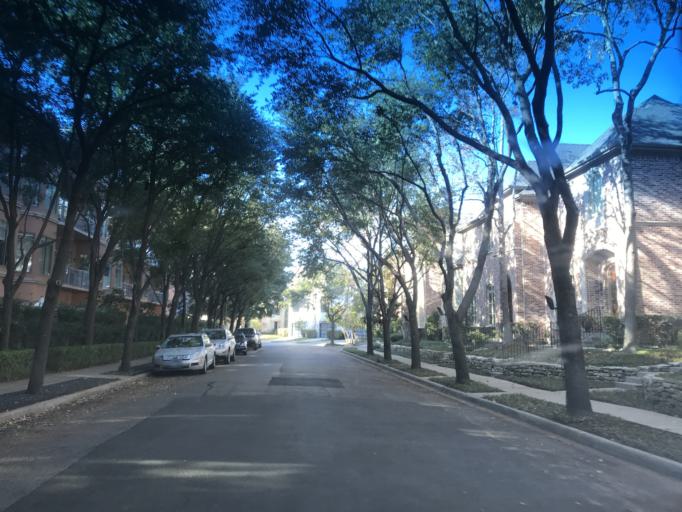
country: US
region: Texas
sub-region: Dallas County
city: Highland Park
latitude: 32.8222
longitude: -96.8119
